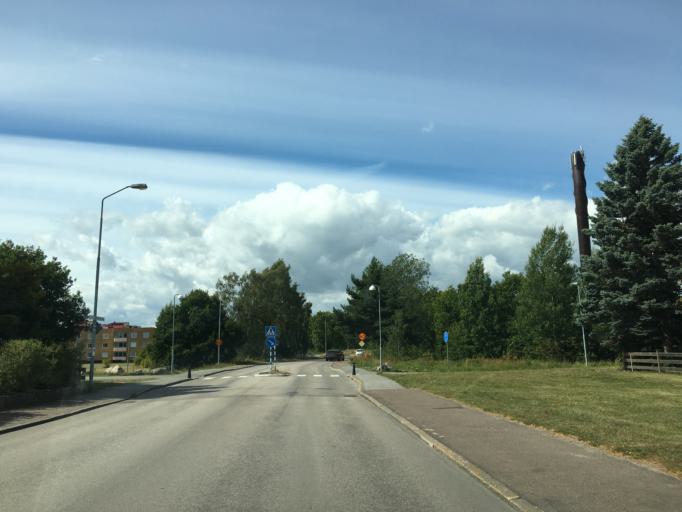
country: SE
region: Kalmar
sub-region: Kalmar Kommun
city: Kalmar
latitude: 56.6981
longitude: 16.3491
